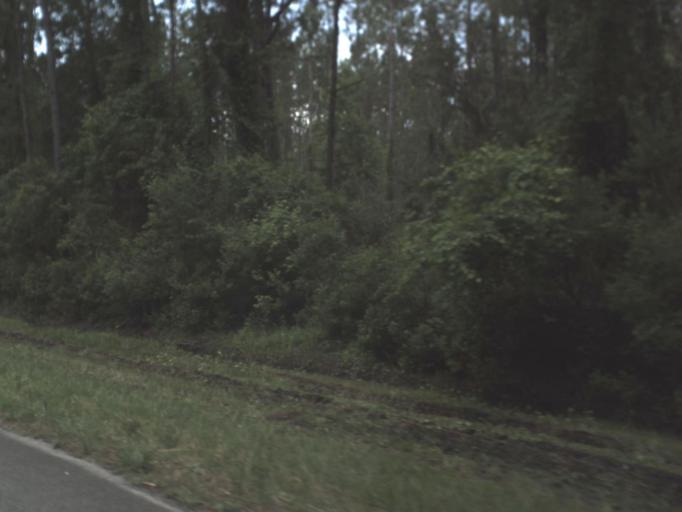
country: US
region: Florida
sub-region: Nassau County
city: Yulee
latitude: 30.6510
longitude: -81.6240
